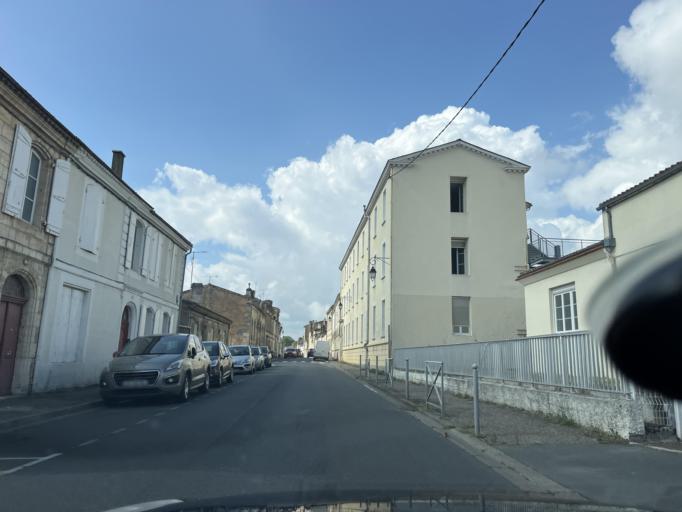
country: FR
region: Aquitaine
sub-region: Departement de la Gironde
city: Blaye
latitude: 45.1347
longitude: -0.6590
